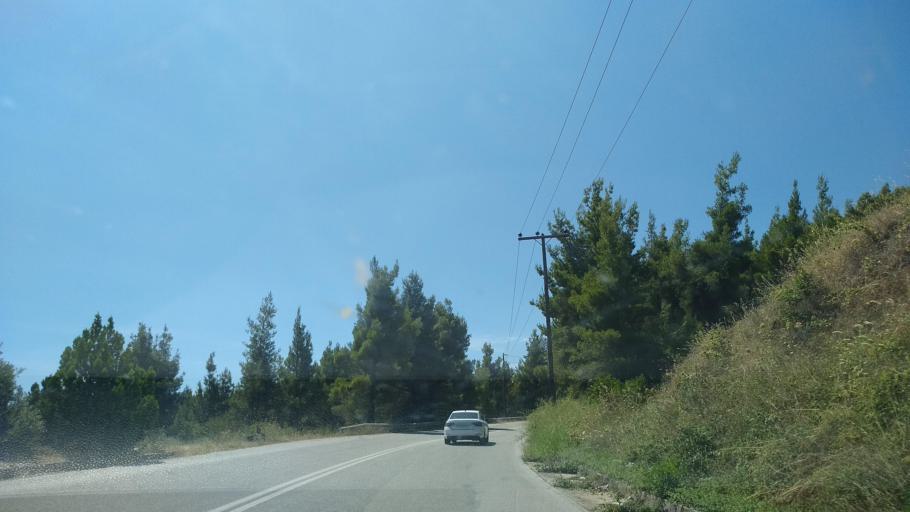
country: GR
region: Central Macedonia
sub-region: Nomos Chalkidikis
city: Agios Nikolaos
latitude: 40.2820
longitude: 23.6848
